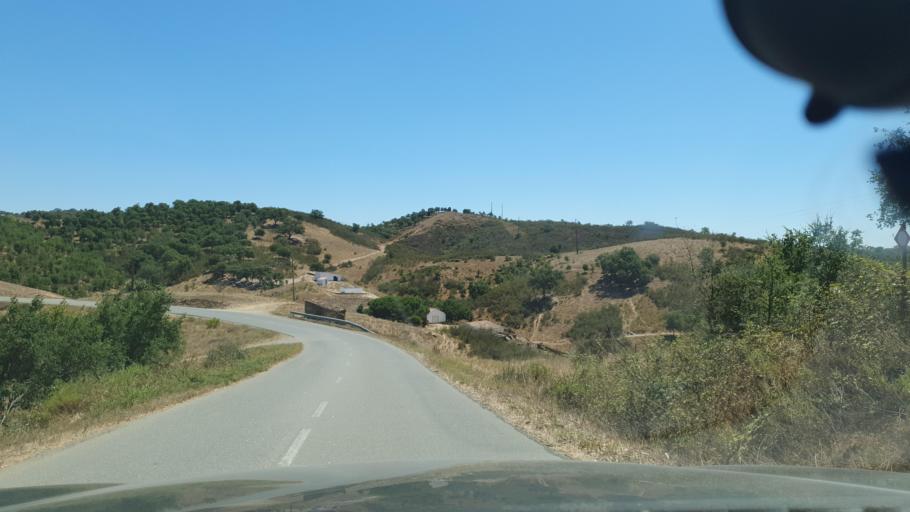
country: PT
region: Beja
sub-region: Odemira
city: Odemira
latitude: 37.5510
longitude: -8.4373
